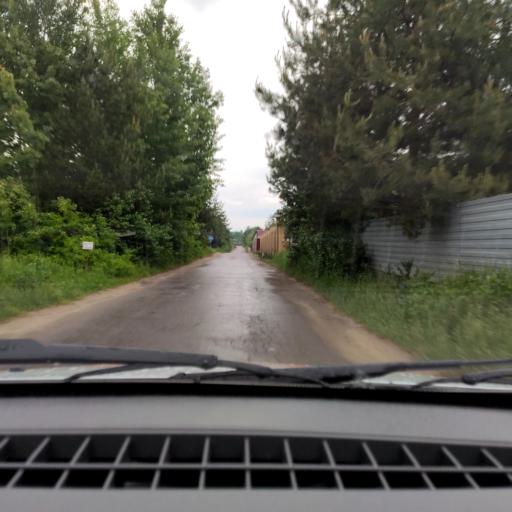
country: RU
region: Voronezj
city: Ramon'
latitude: 51.8553
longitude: 39.2448
